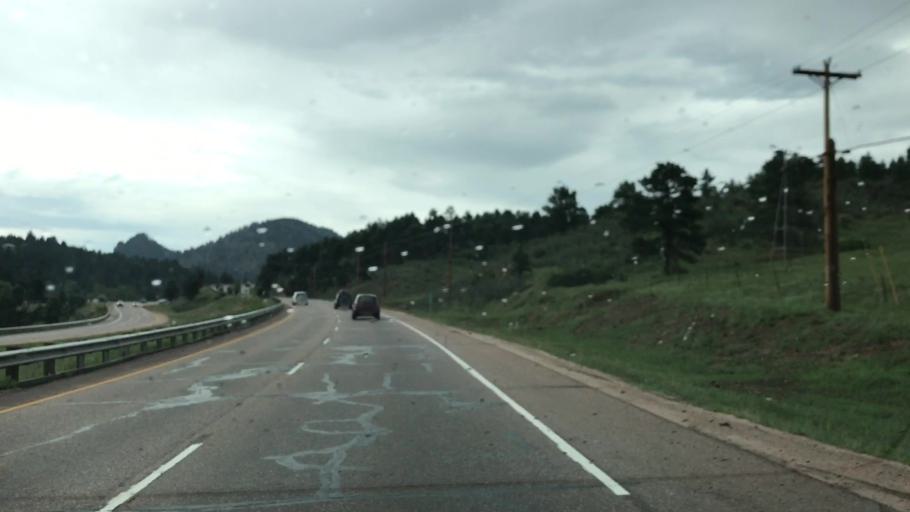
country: US
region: Colorado
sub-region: El Paso County
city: Cascade-Chipita Park
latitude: 38.9464
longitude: -105.0211
